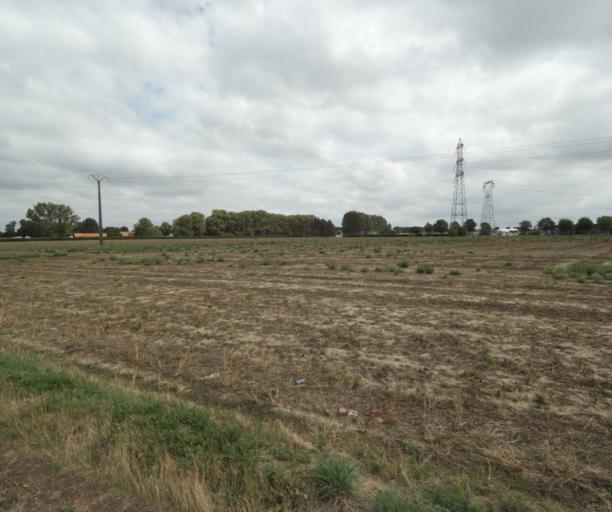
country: FR
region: Nord-Pas-de-Calais
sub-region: Departement du Nord
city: Anstaing
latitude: 50.6114
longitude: 3.1819
